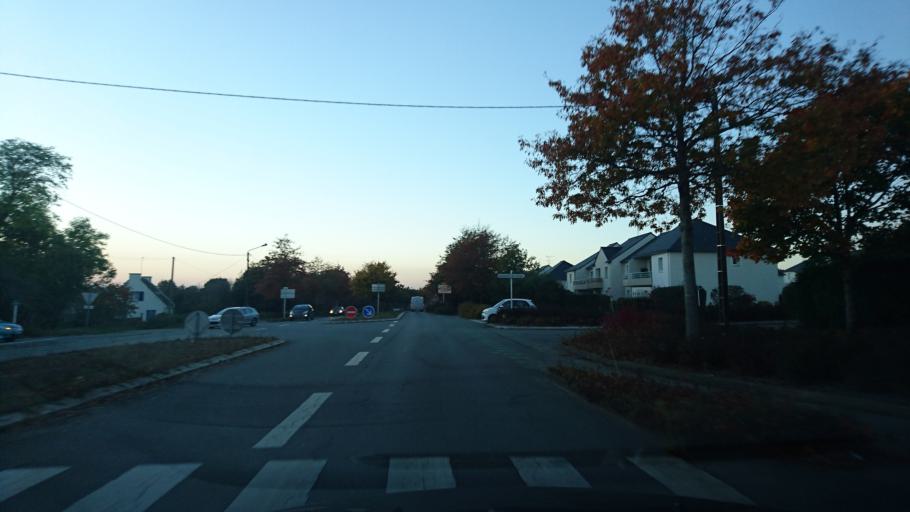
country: FR
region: Brittany
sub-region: Departement du Morbihan
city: Auray
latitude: 47.6801
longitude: -3.0130
